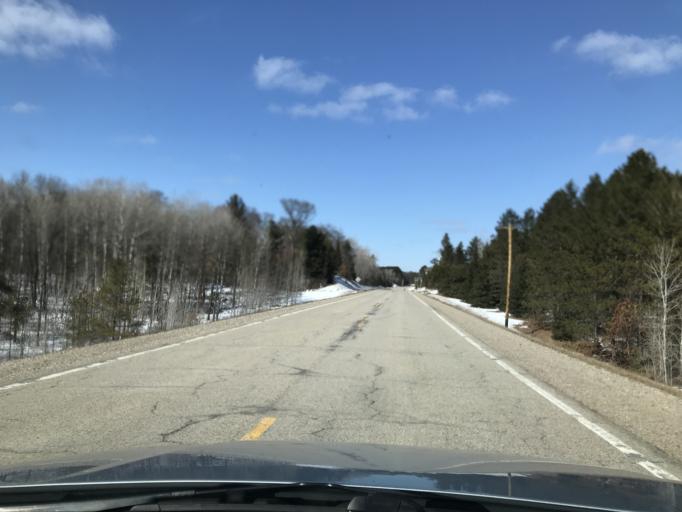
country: US
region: Wisconsin
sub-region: Marinette County
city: Peshtigo
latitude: 45.3268
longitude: -88.1019
